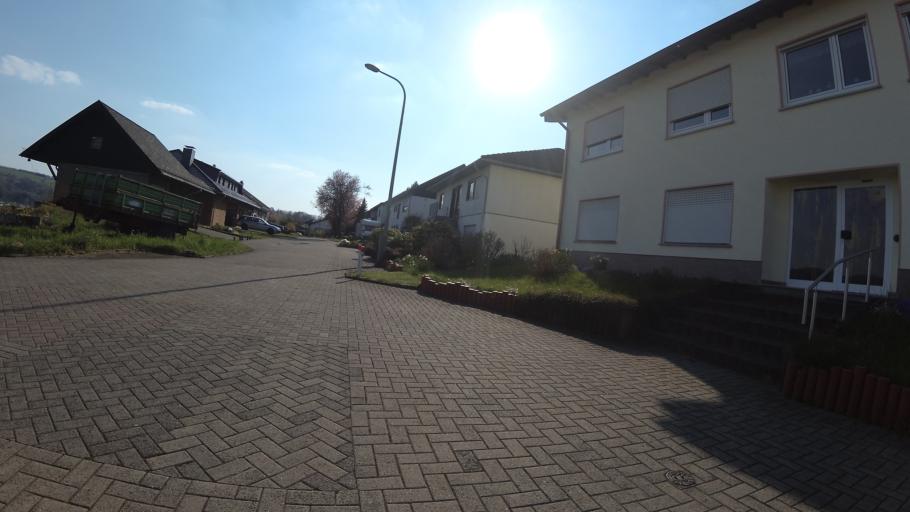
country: DE
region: Rheinland-Pfalz
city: Breitenbach
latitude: 49.4721
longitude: 7.2508
